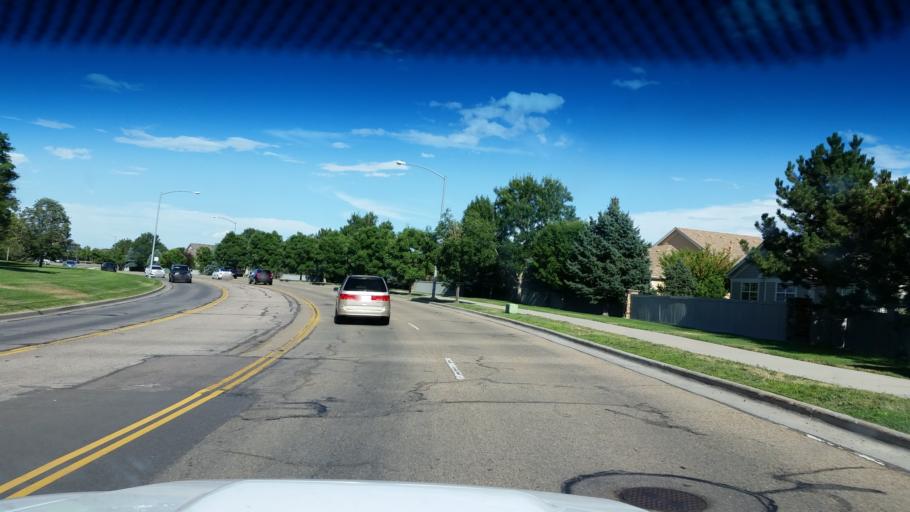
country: US
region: Colorado
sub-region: Adams County
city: Northglenn
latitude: 39.9270
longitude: -104.9466
